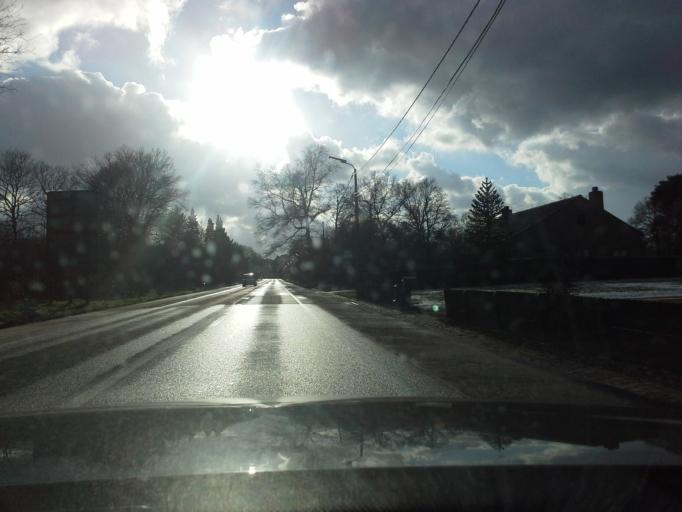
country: BE
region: Flanders
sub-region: Provincie Antwerpen
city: Mol
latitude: 51.1731
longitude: 5.1080
